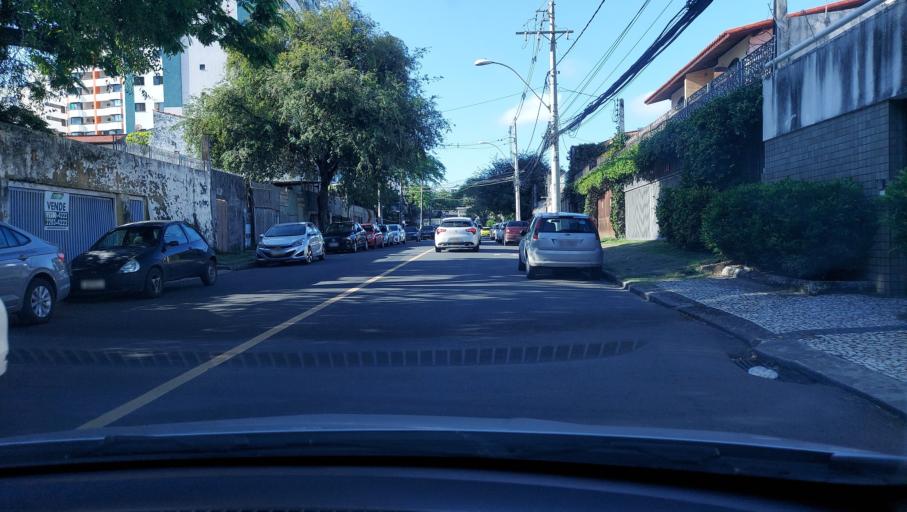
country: BR
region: Bahia
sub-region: Salvador
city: Salvador
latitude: -12.9828
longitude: -38.4603
